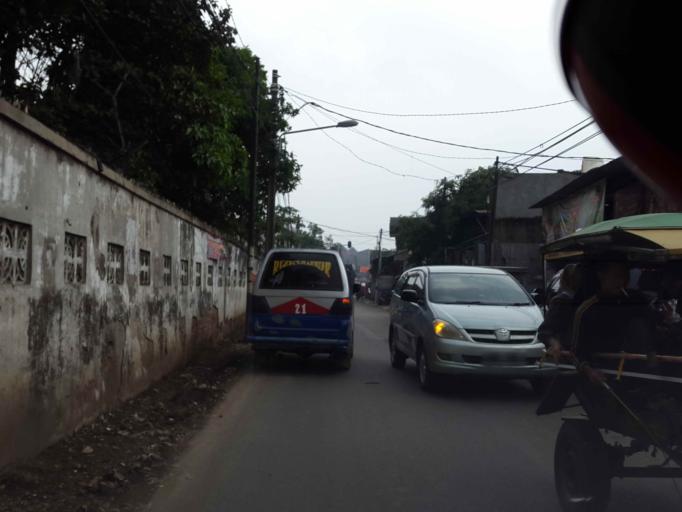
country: ID
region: West Java
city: Cimahi
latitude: -6.8995
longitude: 107.5557
